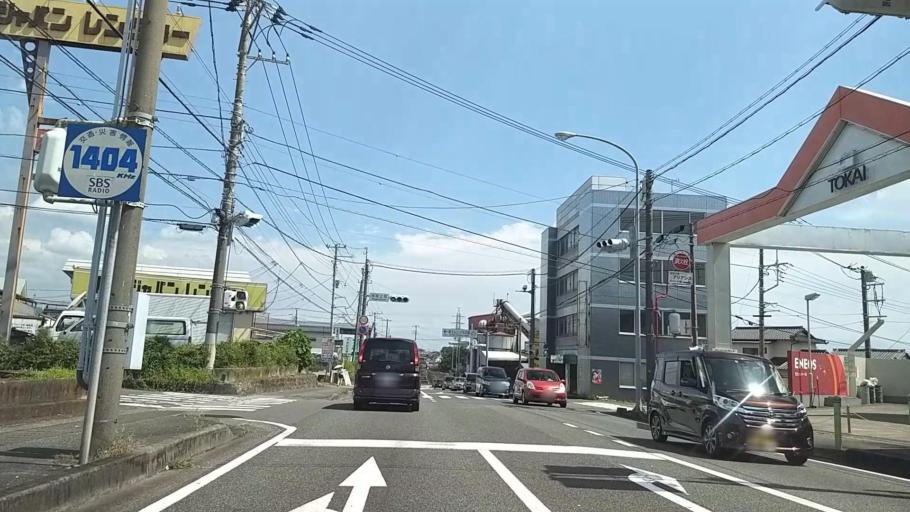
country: JP
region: Shizuoka
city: Fuji
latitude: 35.1719
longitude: 138.6762
